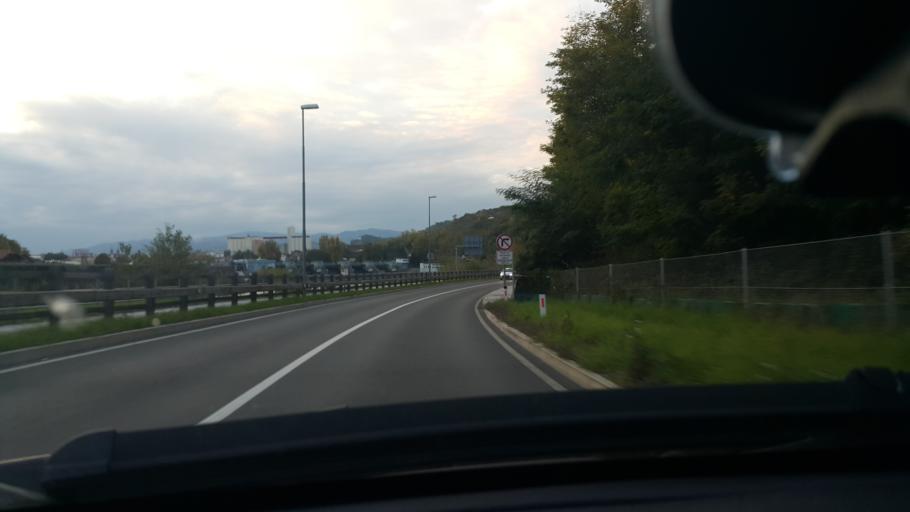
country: SI
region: Maribor
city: Maribor
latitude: 46.5589
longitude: 15.6796
